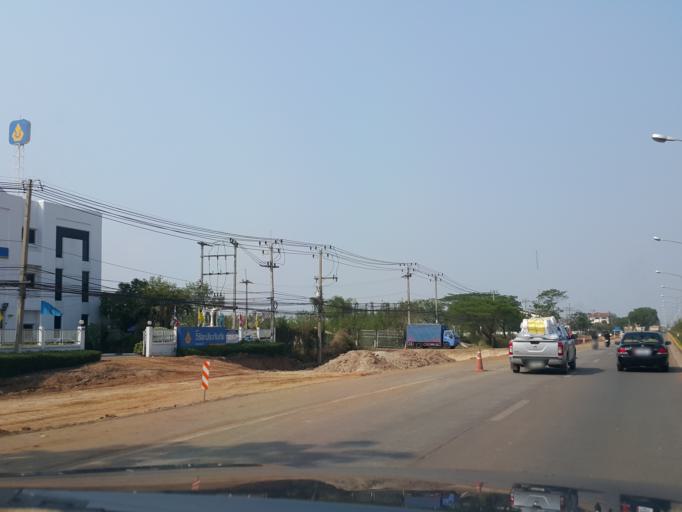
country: TH
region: Lampang
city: Lampang
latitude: 18.2664
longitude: 99.4702
